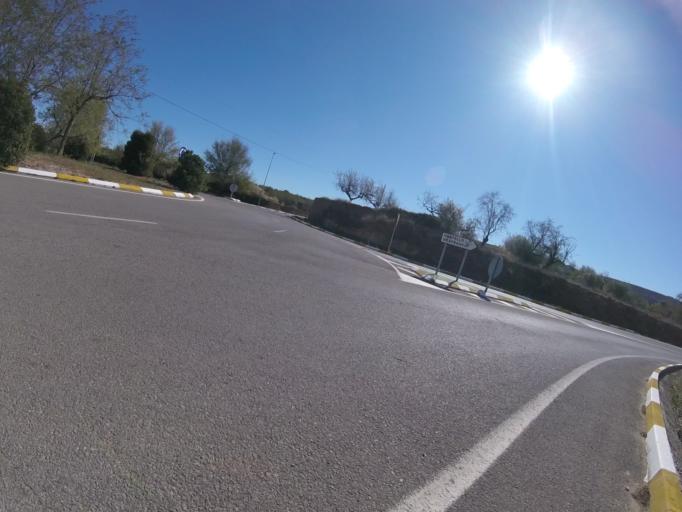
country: ES
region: Valencia
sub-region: Provincia de Castello
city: Albocasser
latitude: 40.3617
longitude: 0.0216
